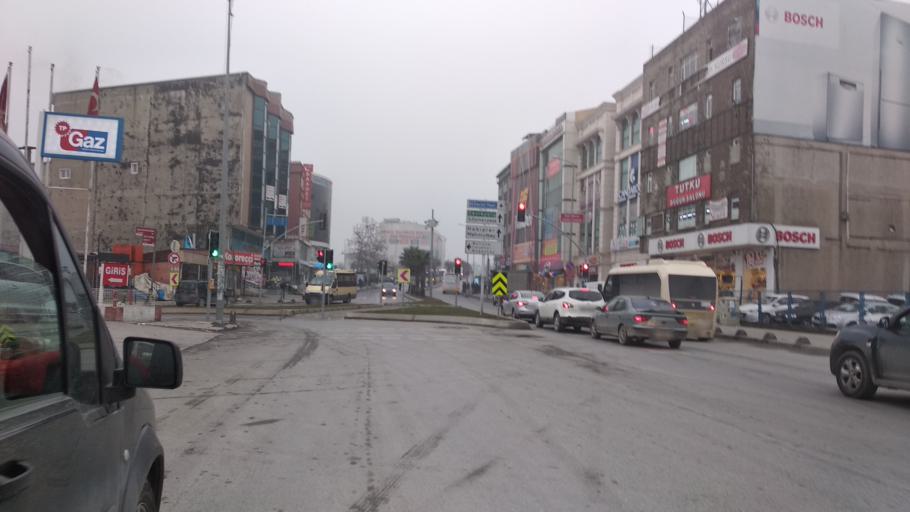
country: TR
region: Istanbul
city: Basaksehir
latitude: 41.1813
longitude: 28.7446
